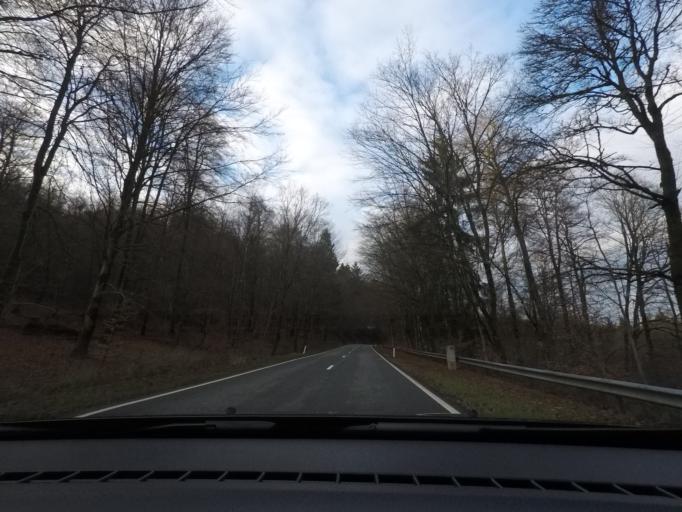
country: BE
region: Wallonia
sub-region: Province du Luxembourg
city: Leglise
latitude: 49.7500
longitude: 5.5240
